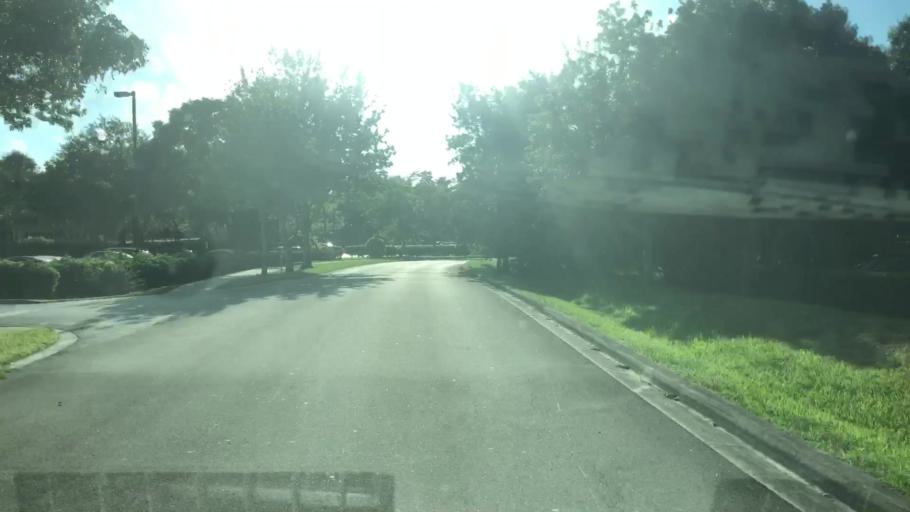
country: US
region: Florida
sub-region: Broward County
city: Kendall Green
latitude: 26.2640
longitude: -80.1450
